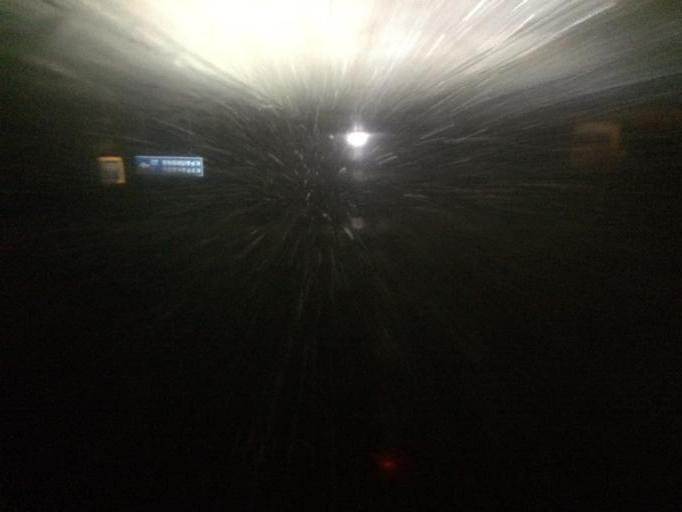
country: RU
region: Tula
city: Krapivna
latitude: 54.1125
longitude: 37.2045
